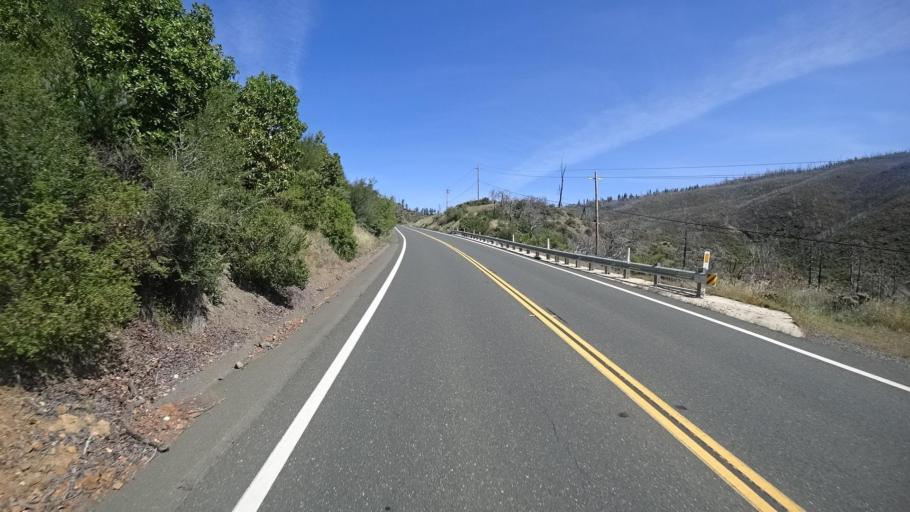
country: US
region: California
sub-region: Lake County
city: Cobb
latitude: 38.7973
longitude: -122.7040
